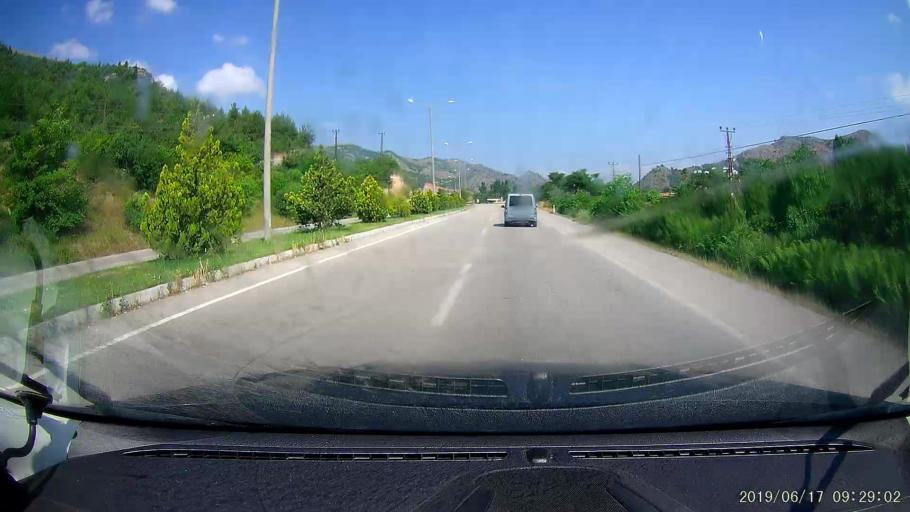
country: TR
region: Amasya
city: Amasya
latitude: 40.6941
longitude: 35.8174
